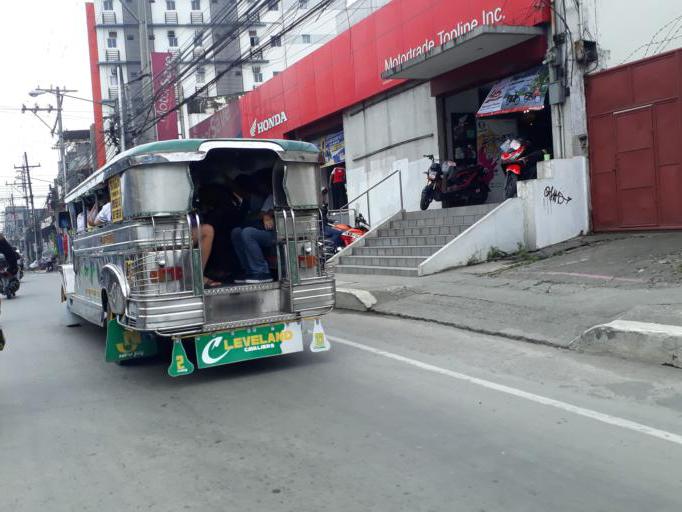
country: PH
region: Calabarzon
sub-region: Province of Rizal
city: Valenzuela
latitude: 14.6762
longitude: 120.9808
